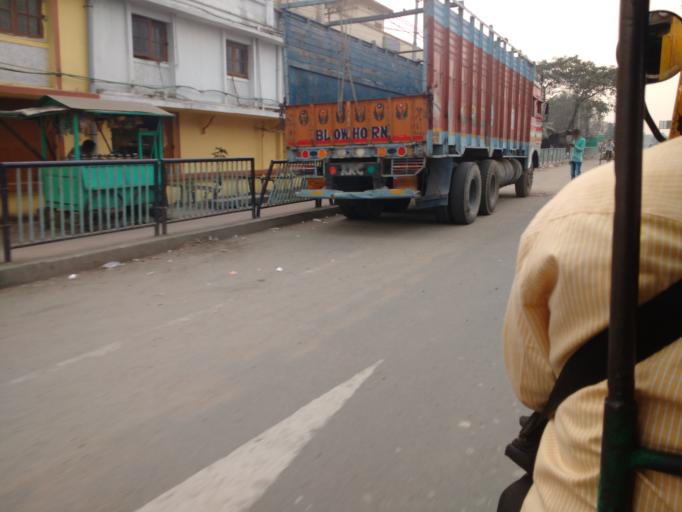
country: IN
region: West Bengal
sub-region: North 24 Parganas
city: Baranagar
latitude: 22.6520
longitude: 88.3715
